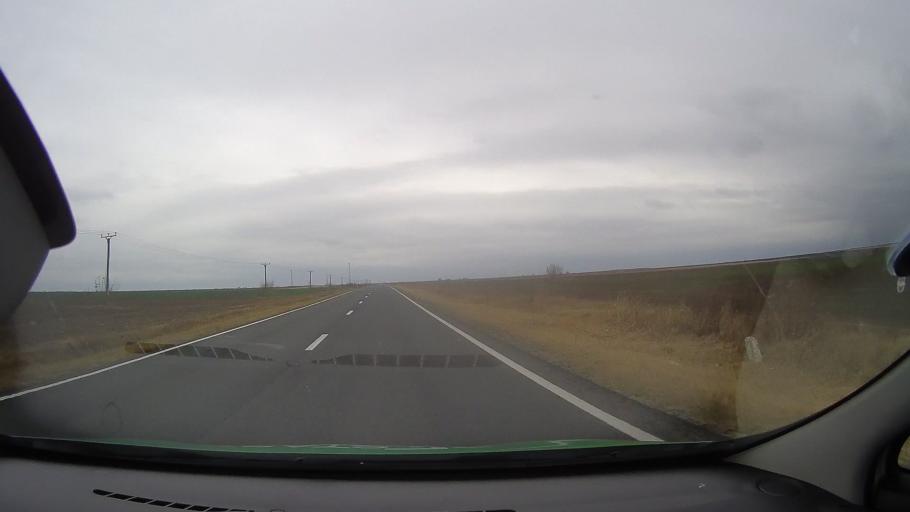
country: RO
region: Constanta
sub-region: Comuna Nicolae Balcescu
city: Nicolae Balcescu
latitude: 44.3779
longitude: 28.4157
